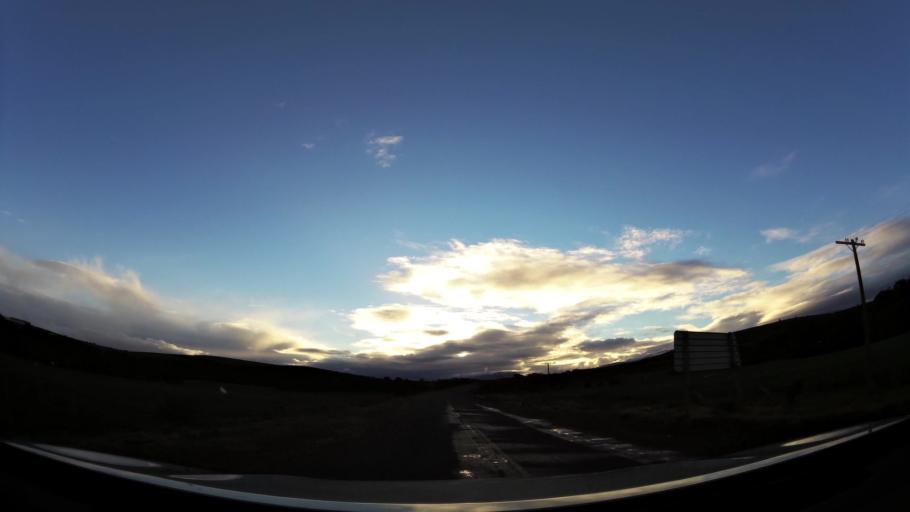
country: ZA
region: Western Cape
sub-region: Eden District Municipality
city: Riversdale
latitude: -34.0728
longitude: 20.9075
